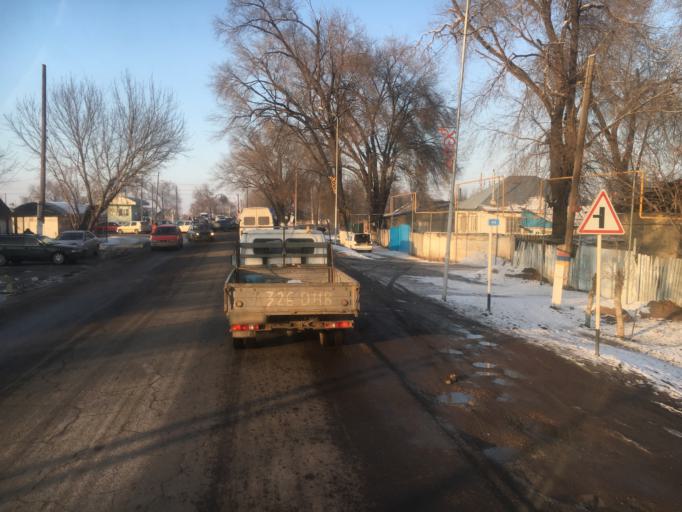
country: KZ
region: Almaty Oblysy
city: Burunday
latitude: 43.3754
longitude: 76.6420
